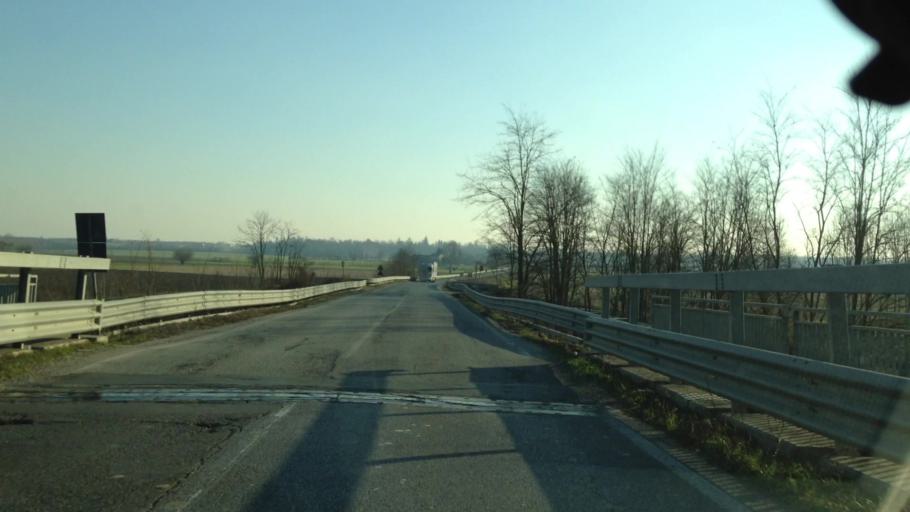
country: IT
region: Piedmont
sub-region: Provincia di Alessandria
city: Felizzano
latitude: 44.8894
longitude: 8.4396
